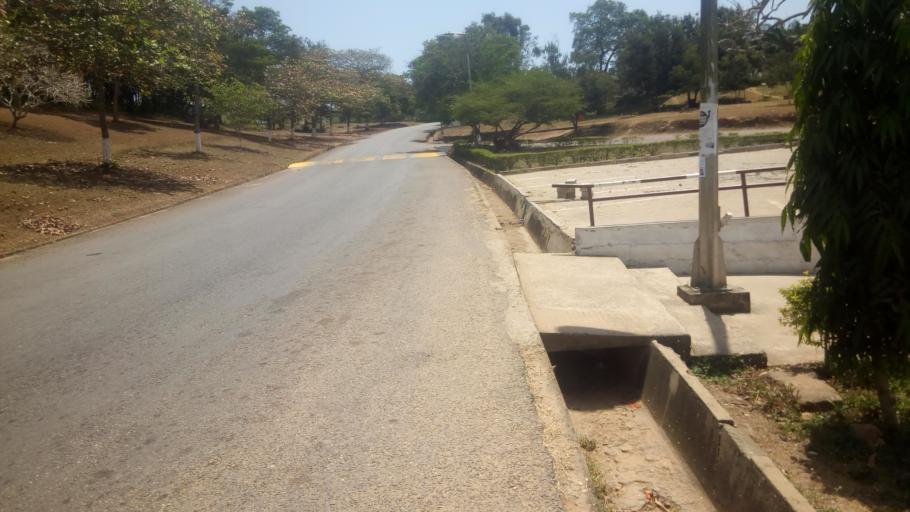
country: GH
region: Central
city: Cape Coast
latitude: 5.1066
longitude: -1.2841
